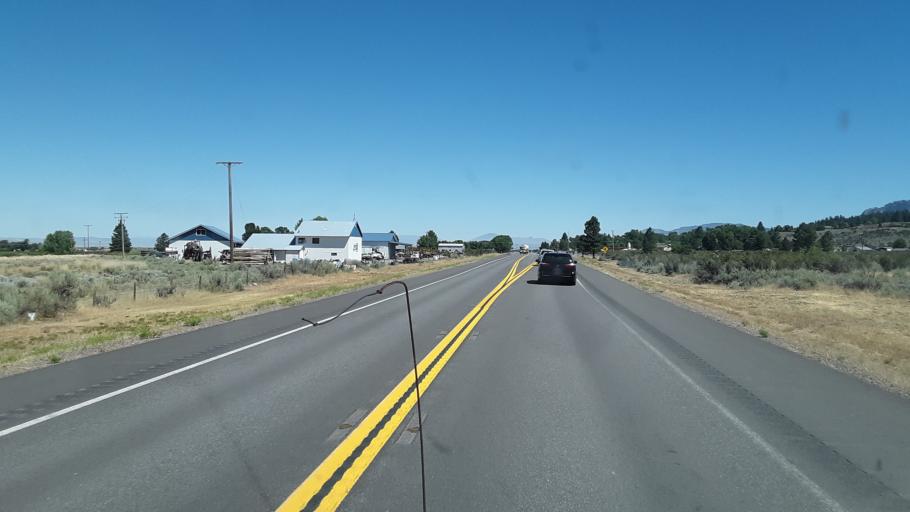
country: US
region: California
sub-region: Lassen County
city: Janesville
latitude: 40.2963
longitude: -120.5122
